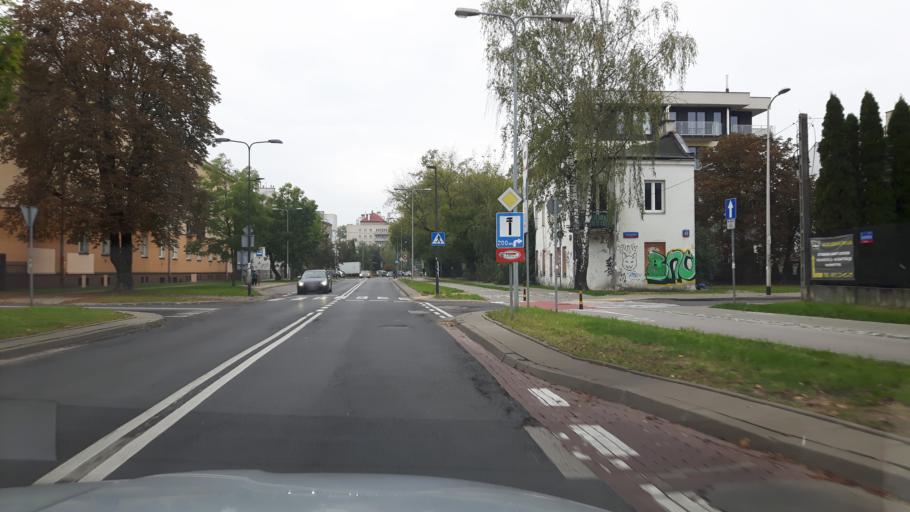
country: PL
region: Masovian Voivodeship
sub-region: Warszawa
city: Praga Poludnie
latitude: 52.2450
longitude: 21.1107
